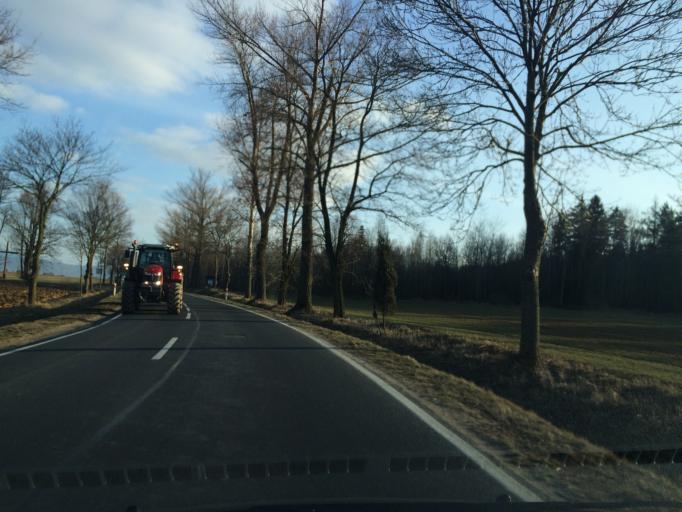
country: PL
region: Lower Silesian Voivodeship
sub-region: Powiat klodzki
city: Bystrzyca Klodzka
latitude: 50.2386
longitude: 16.6743
